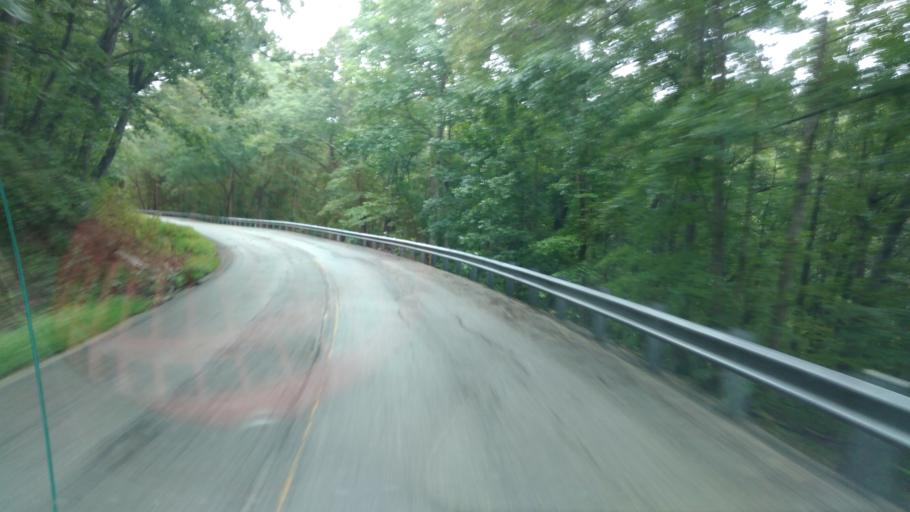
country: US
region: Kentucky
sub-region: Fleming County
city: Flemingsburg
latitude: 38.4522
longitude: -83.5215
